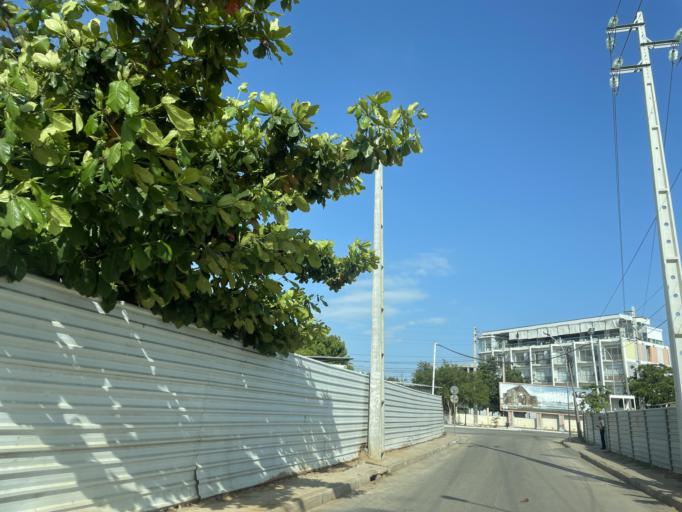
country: AO
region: Luanda
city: Luanda
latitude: -8.9095
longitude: 13.1810
